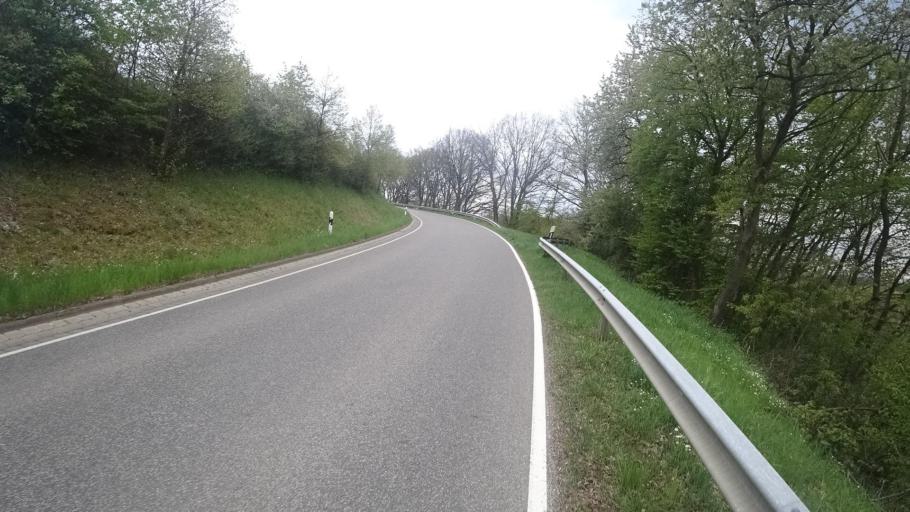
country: DE
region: Rheinland-Pfalz
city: Niederkumbd
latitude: 50.0047
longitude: 7.5356
